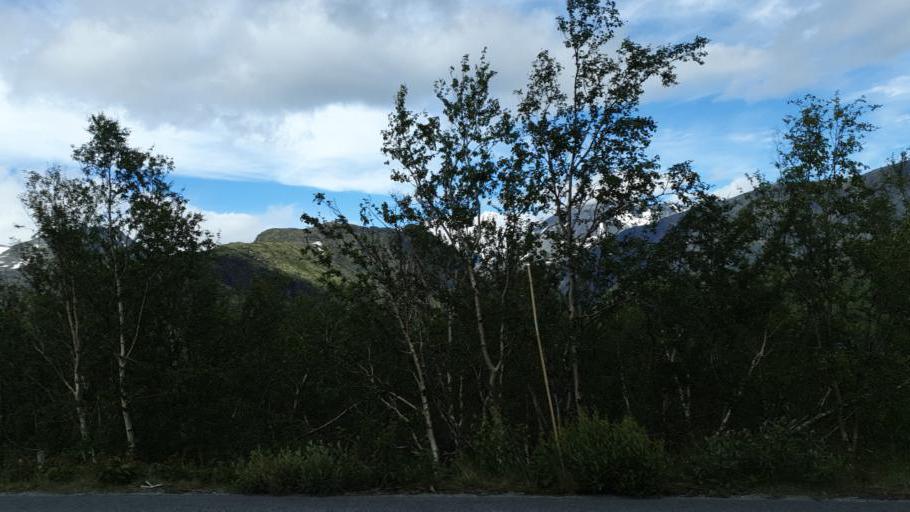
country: NO
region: Oppland
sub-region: Oystre Slidre
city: Heggenes
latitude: 61.4669
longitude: 8.8124
